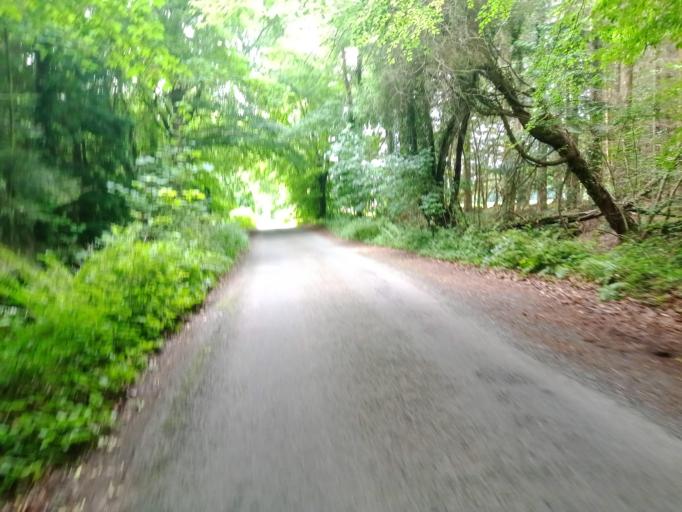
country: IE
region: Leinster
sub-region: Laois
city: Abbeyleix
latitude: 52.8995
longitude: -7.3612
